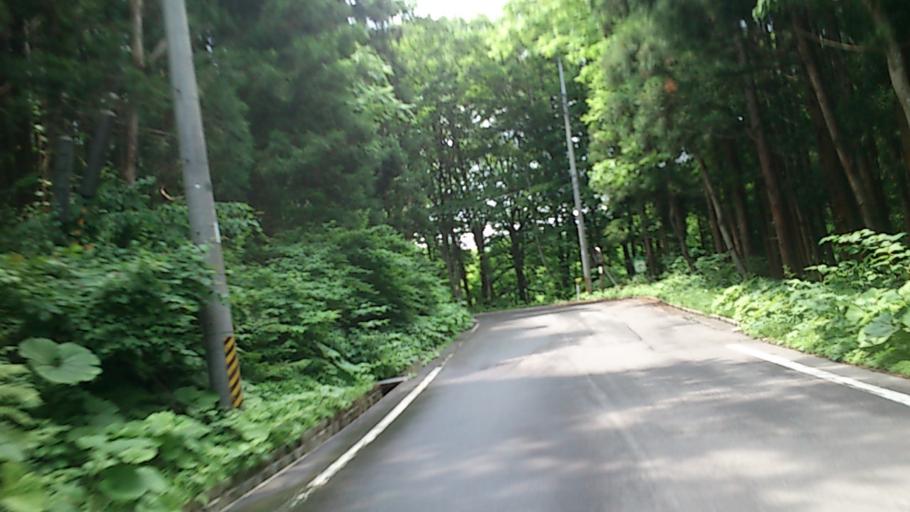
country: JP
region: Aomori
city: Hirosaki
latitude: 40.5186
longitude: 140.1981
